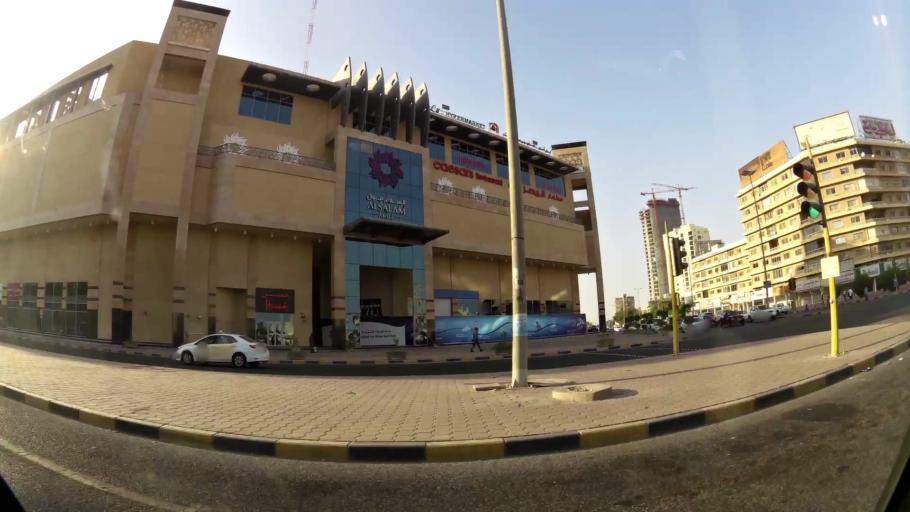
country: KW
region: Muhafazat Hawalli
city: As Salimiyah
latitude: 29.3355
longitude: 48.0637
